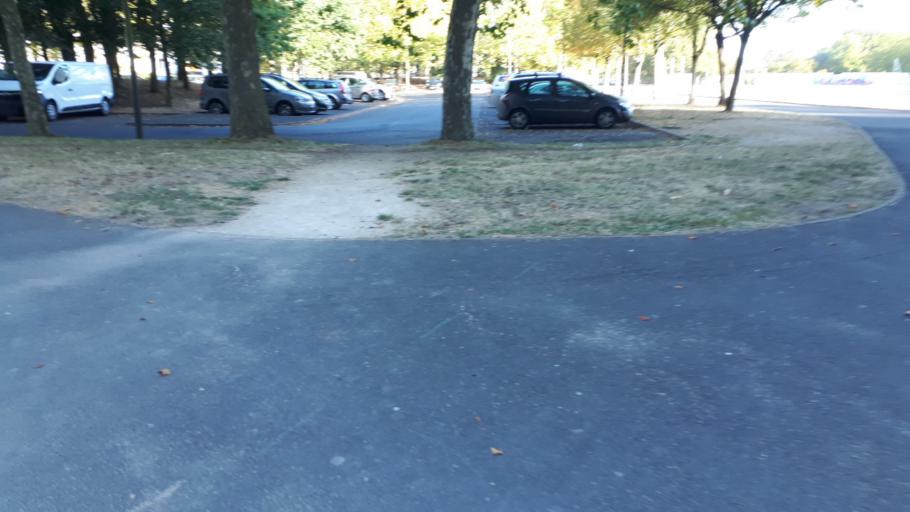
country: FR
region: Centre
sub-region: Departement du Loir-et-Cher
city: Blois
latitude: 47.5909
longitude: 1.3034
